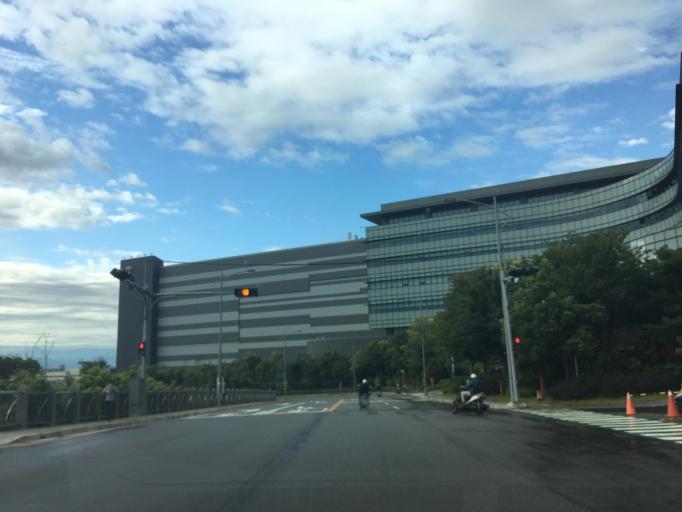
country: TW
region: Taiwan
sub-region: Taichung City
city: Taichung
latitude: 24.2115
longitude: 120.6090
